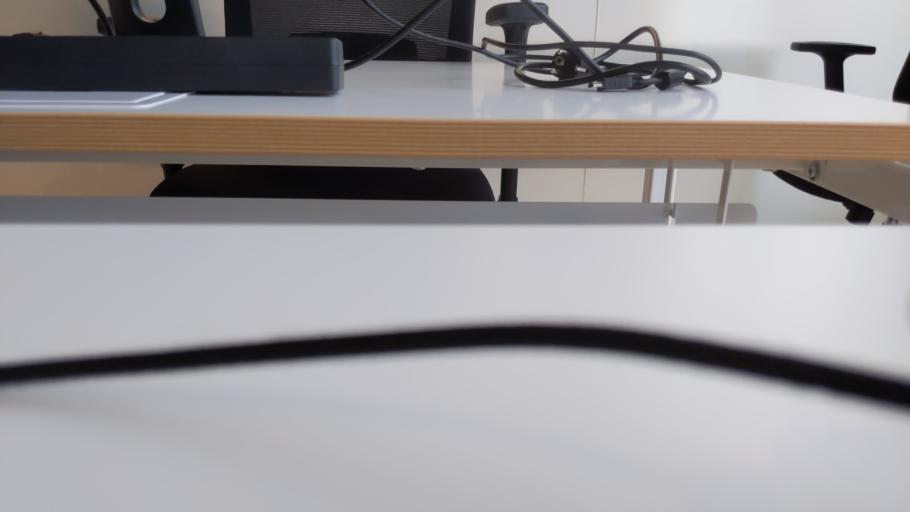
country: RU
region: Moskovskaya
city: Shevlyakovo
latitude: 56.4219
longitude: 37.0004
